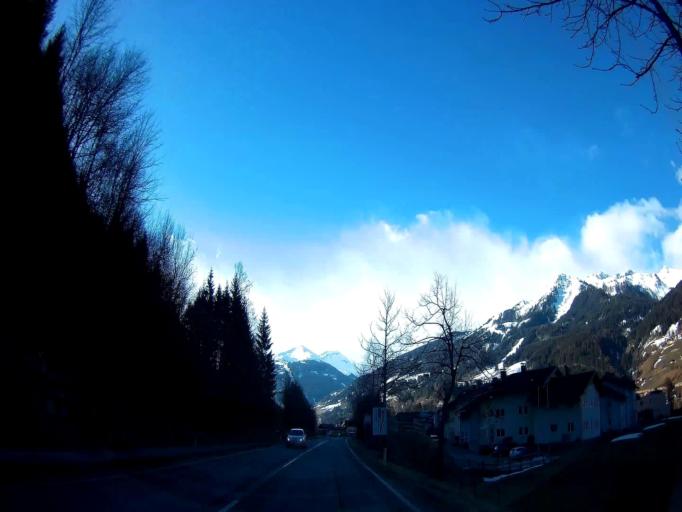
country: AT
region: Salzburg
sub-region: Politischer Bezirk Sankt Johann im Pongau
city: Bad Hofgastein
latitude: 47.1879
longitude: 13.1013
